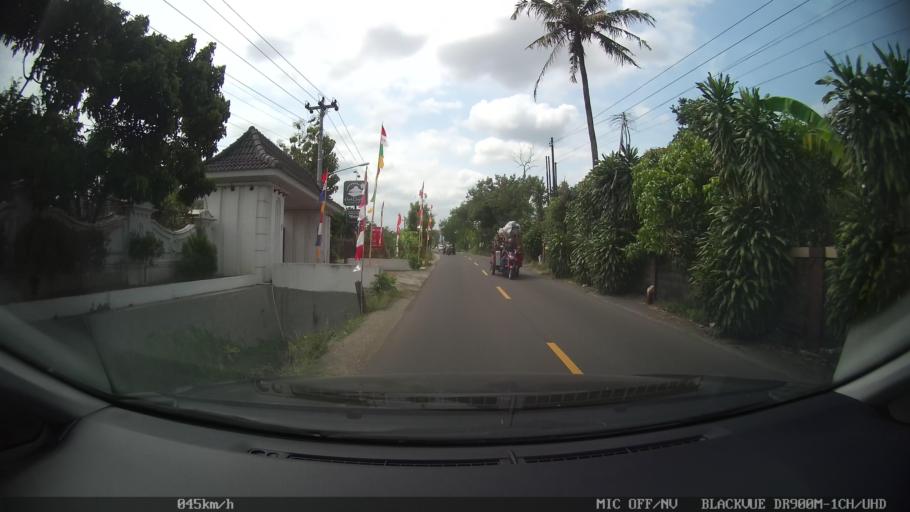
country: ID
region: Central Java
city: Candi Prambanan
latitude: -7.7445
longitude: 110.4813
